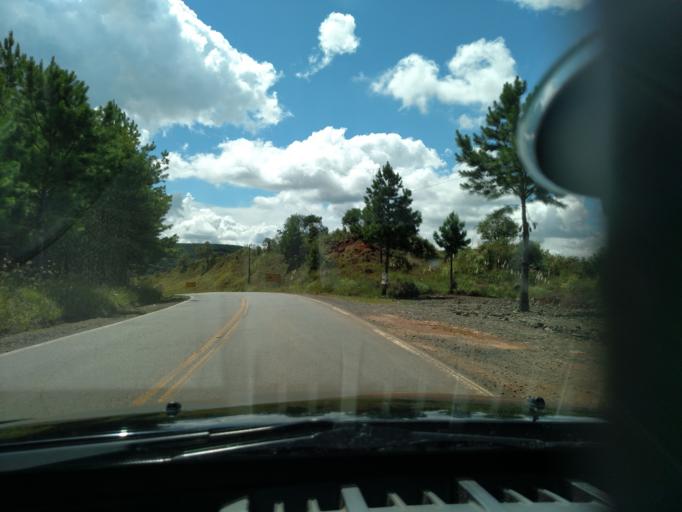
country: BR
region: Santa Catarina
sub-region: Lages
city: Lages
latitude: -27.8688
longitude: -50.1814
